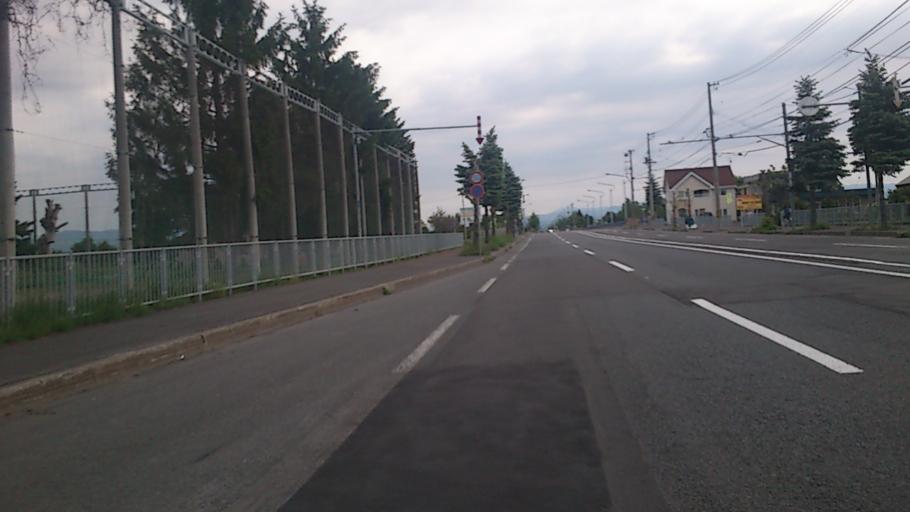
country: JP
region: Hokkaido
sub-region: Asahikawa-shi
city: Asahikawa
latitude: 43.8200
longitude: 142.4488
